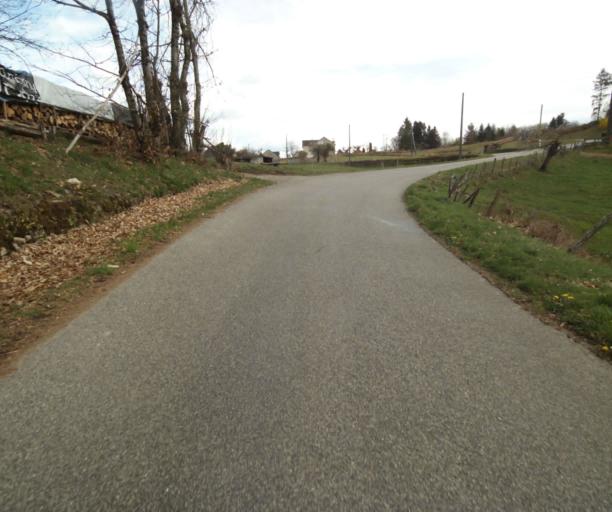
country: FR
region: Limousin
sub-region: Departement de la Correze
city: Argentat
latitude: 45.1935
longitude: 1.9573
